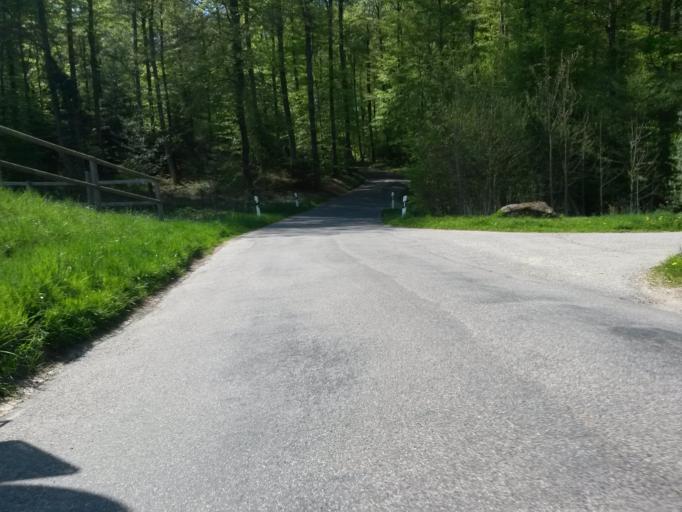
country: CH
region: Bern
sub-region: Oberaargau
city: Herzogenbuchsee
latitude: 47.1985
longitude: 7.7320
